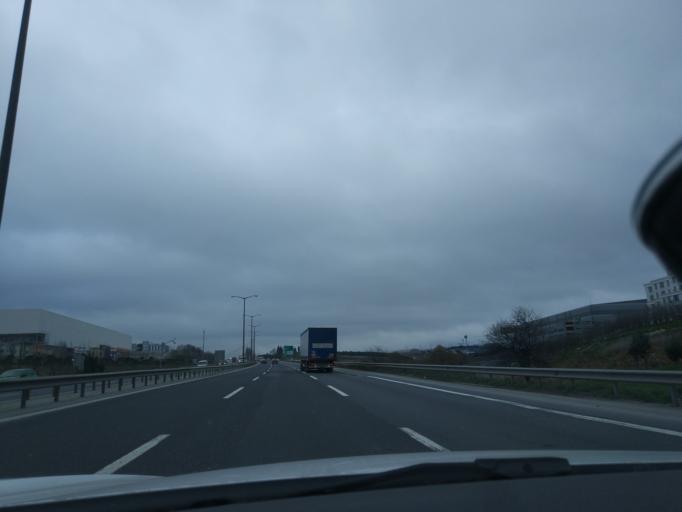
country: TR
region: Istanbul
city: Esenyurt
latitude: 41.0741
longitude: 28.6472
